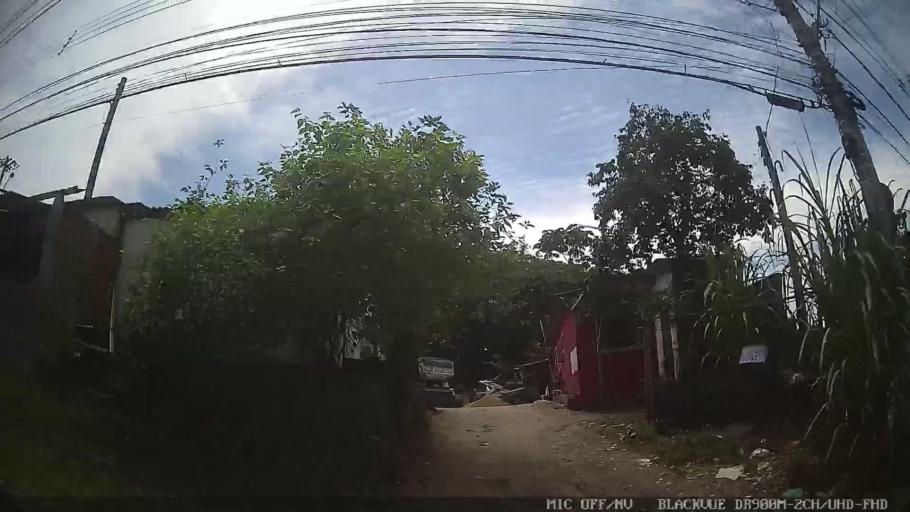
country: BR
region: Sao Paulo
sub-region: Santa Isabel
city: Santa Isabel
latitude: -23.4107
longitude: -46.2064
